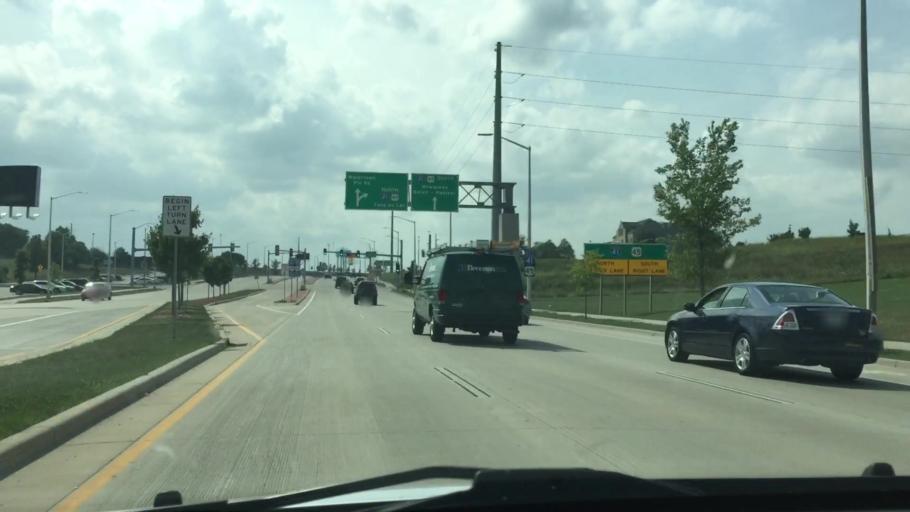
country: US
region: Wisconsin
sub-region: Milwaukee County
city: Wauwatosa
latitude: 43.0452
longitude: -88.0277
